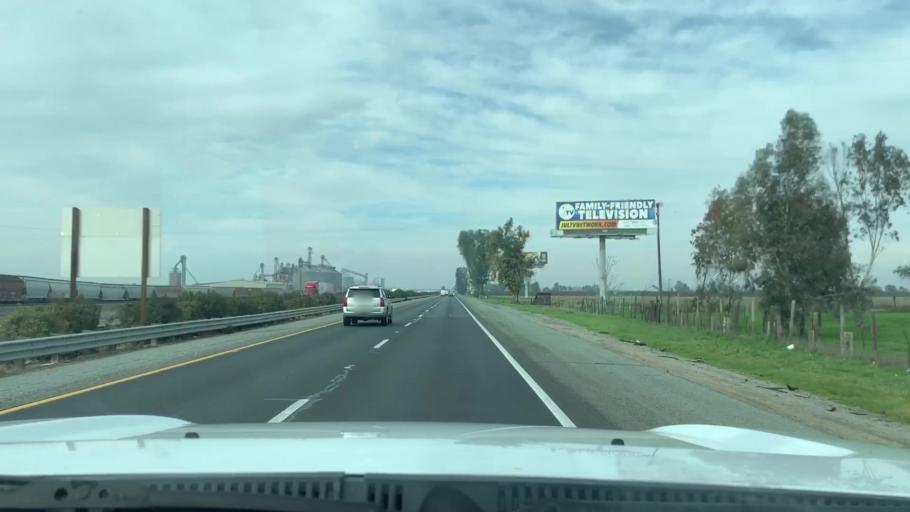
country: US
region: California
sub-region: Tulare County
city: Pixley
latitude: 35.9916
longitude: -119.3003
